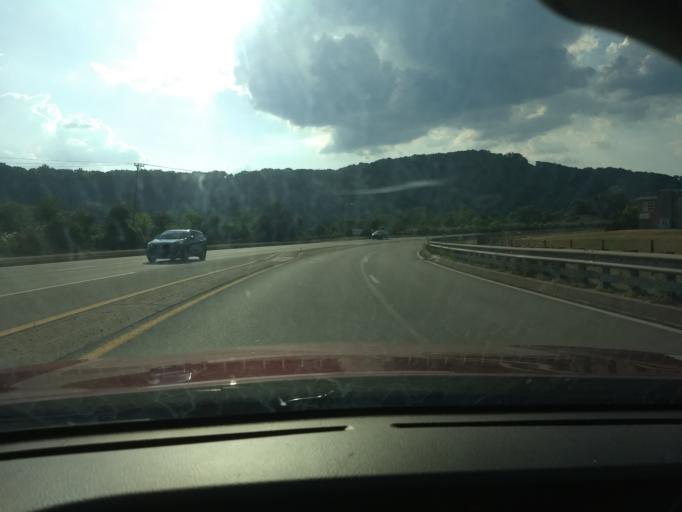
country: US
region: Pennsylvania
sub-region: Westmoreland County
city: Lower Burrell
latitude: 40.5533
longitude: -79.7632
